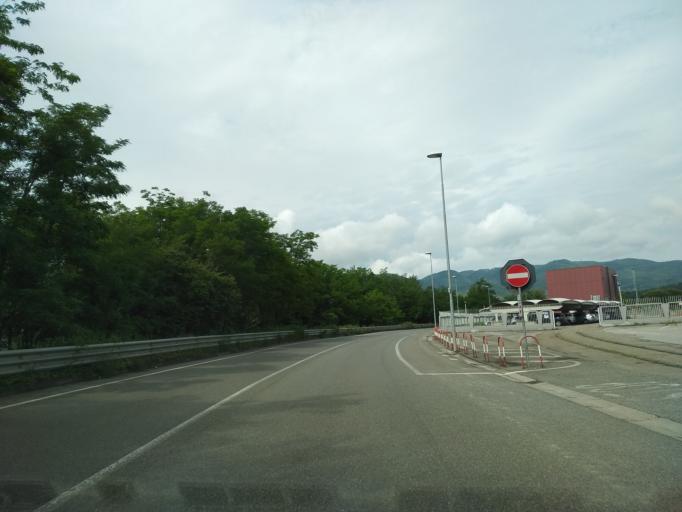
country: IT
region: Tuscany
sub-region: Province of Arezzo
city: San Cipriano-S.Barbara-Centinale
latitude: 43.5631
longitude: 11.4789
